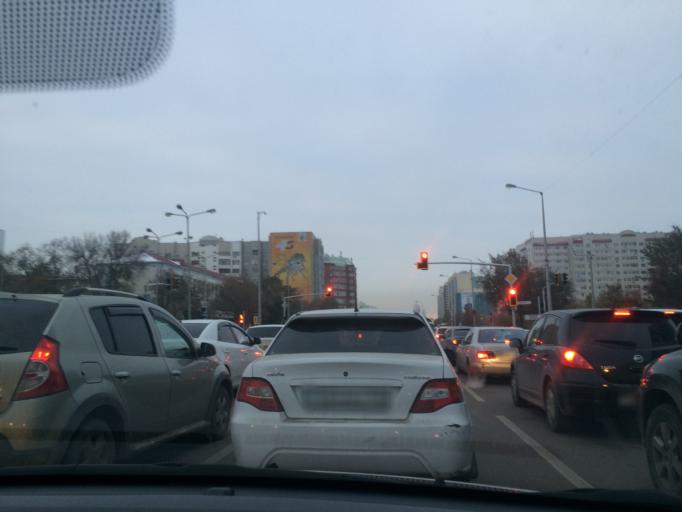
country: KZ
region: Astana Qalasy
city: Astana
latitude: 51.1667
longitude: 71.4086
